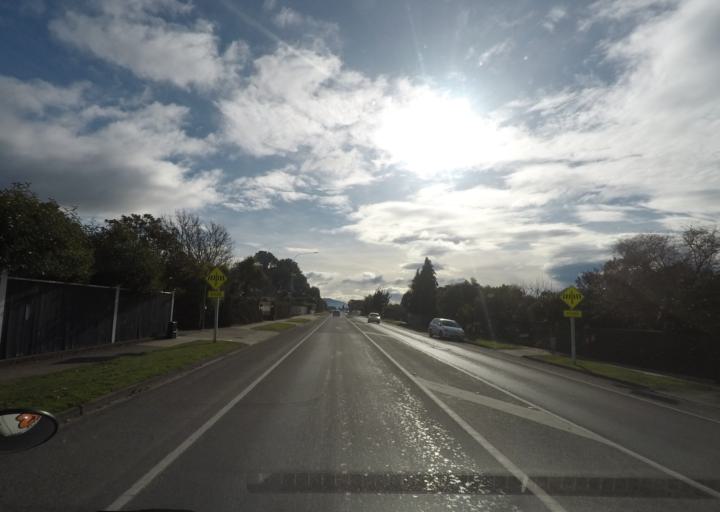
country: NZ
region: Tasman
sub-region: Tasman District
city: Motueka
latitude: -41.1282
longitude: 173.0103
